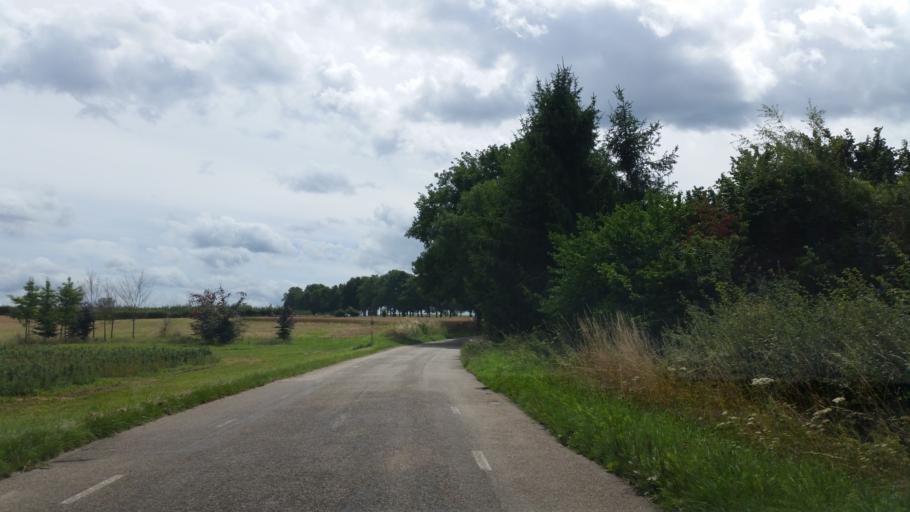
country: NL
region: Limburg
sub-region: Eijsden-Margraten
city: Margraten
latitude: 50.8288
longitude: 5.8025
